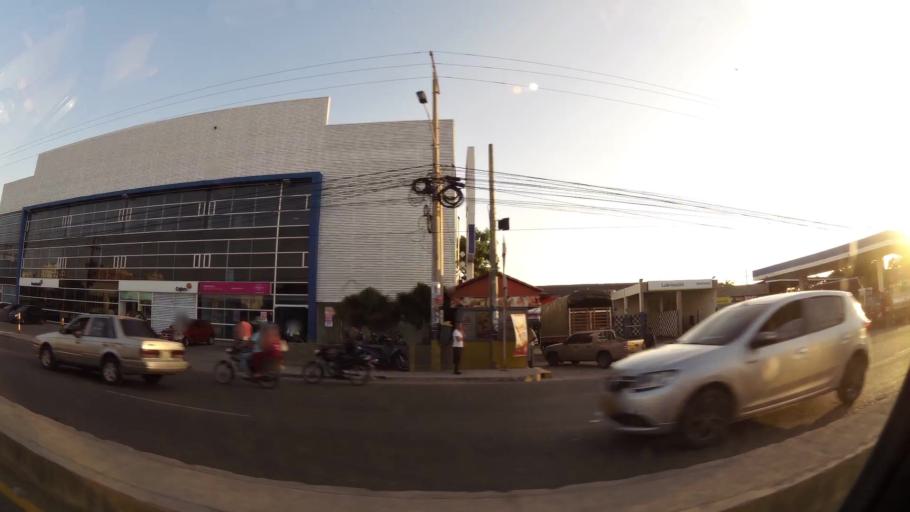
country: CO
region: Bolivar
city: Cartagena
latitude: 10.3887
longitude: -75.5203
